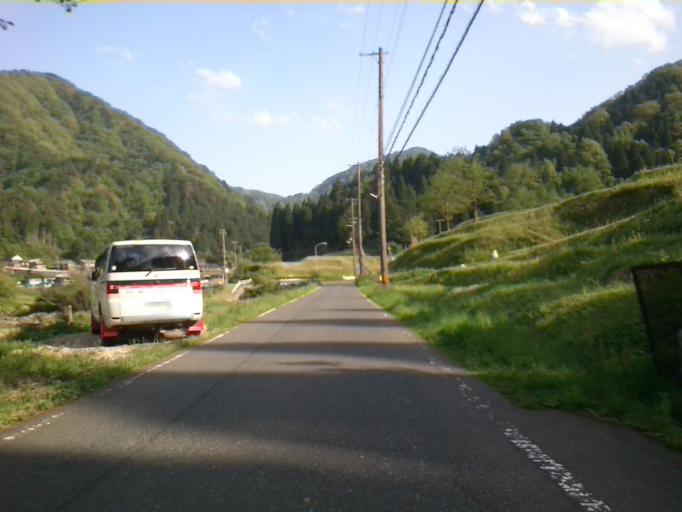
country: JP
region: Kyoto
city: Miyazu
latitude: 35.6819
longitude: 135.1580
